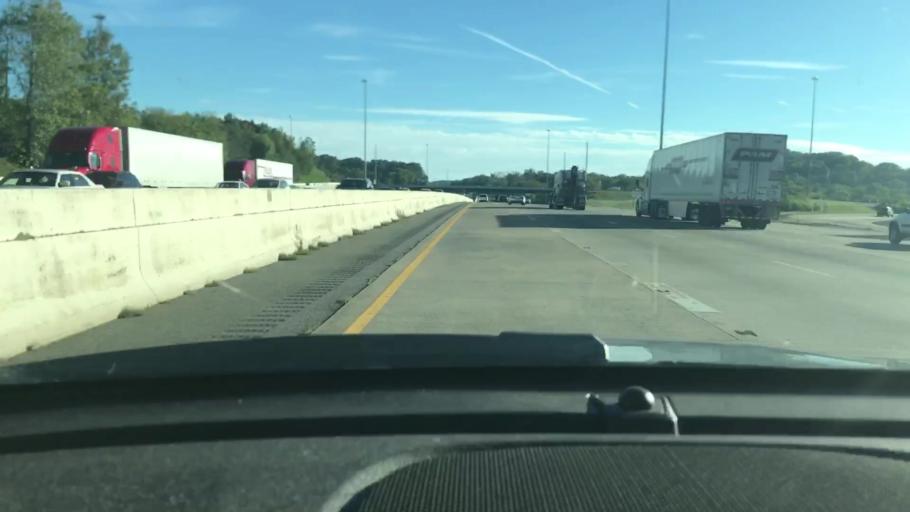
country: US
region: Tennessee
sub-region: Davidson County
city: Goodlettsville
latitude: 36.2683
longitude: -86.7366
